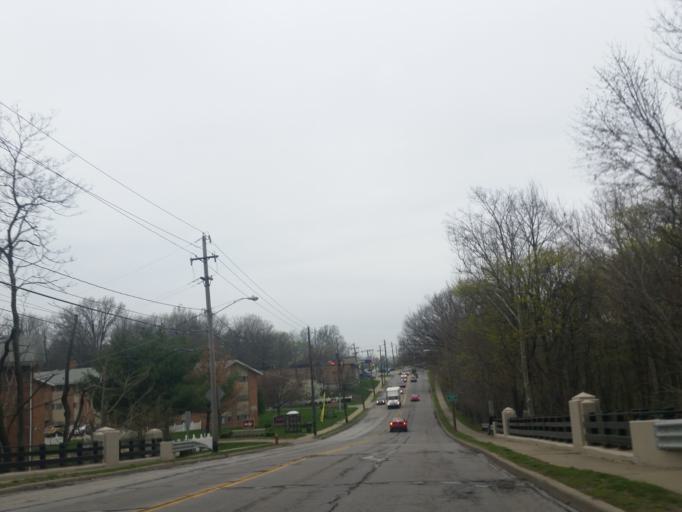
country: US
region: Ohio
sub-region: Cuyahoga County
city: Brooklyn
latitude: 41.4402
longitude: -81.7518
